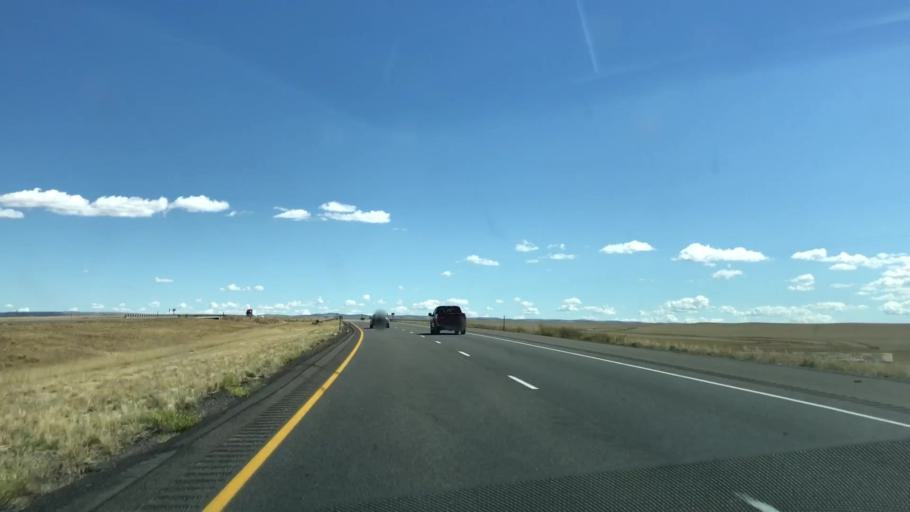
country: US
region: Wyoming
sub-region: Albany County
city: Laramie
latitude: 41.3549
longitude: -105.7451
